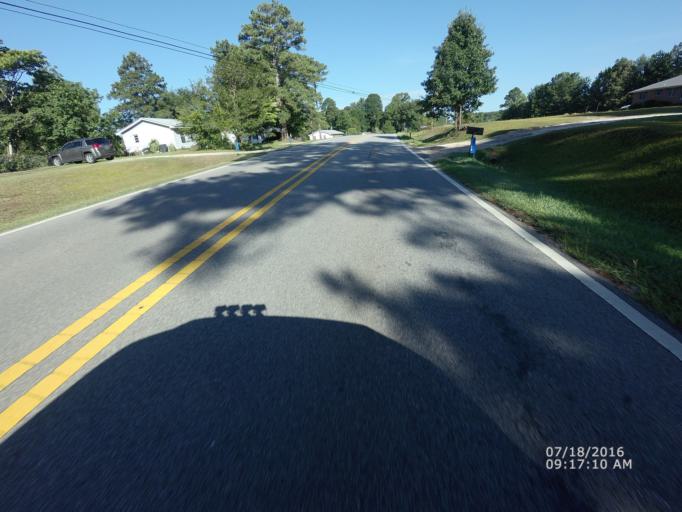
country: US
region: Alabama
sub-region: Chambers County
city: Huguley
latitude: 32.8525
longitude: -85.2722
